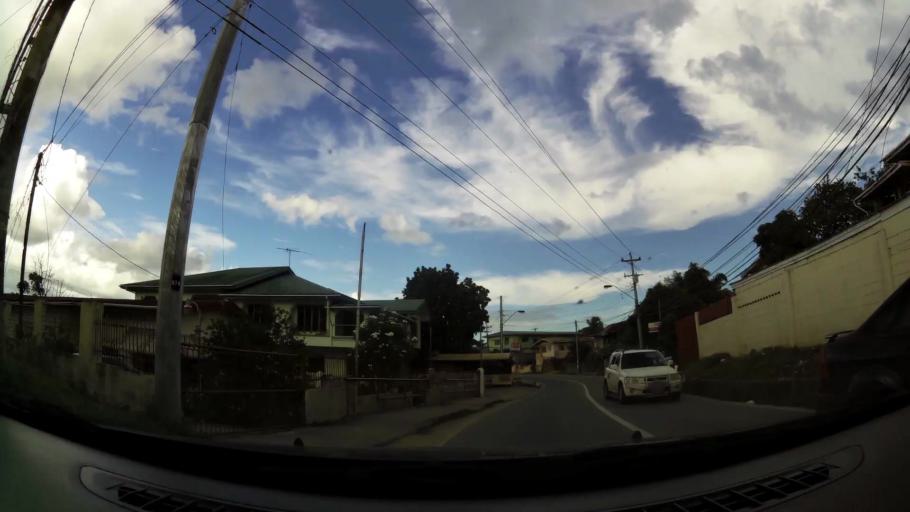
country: TT
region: City of San Fernando
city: Mon Repos
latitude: 10.2767
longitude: -61.4396
